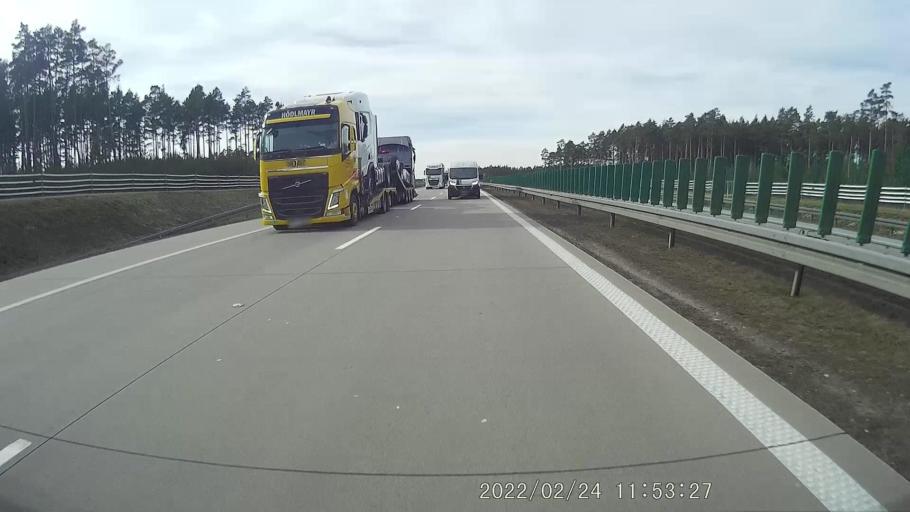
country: PL
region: Lower Silesian Voivodeship
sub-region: Powiat polkowicki
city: Radwanice
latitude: 51.6301
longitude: 15.9765
